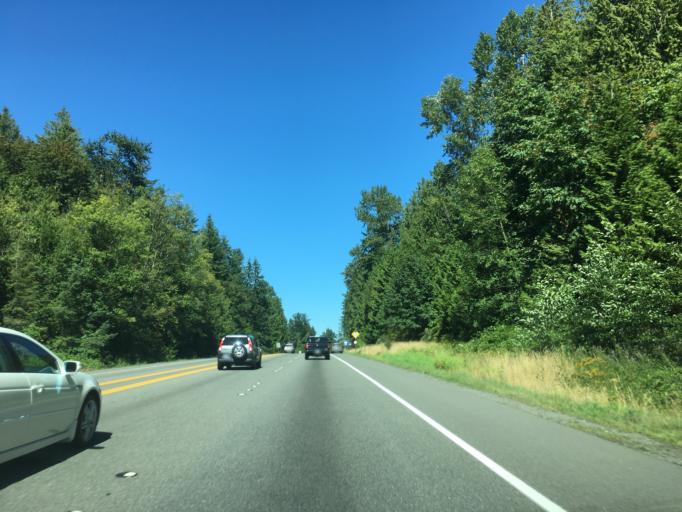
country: US
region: Washington
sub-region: Snohomish County
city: West Lake Stevens
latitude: 47.9957
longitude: -122.1204
